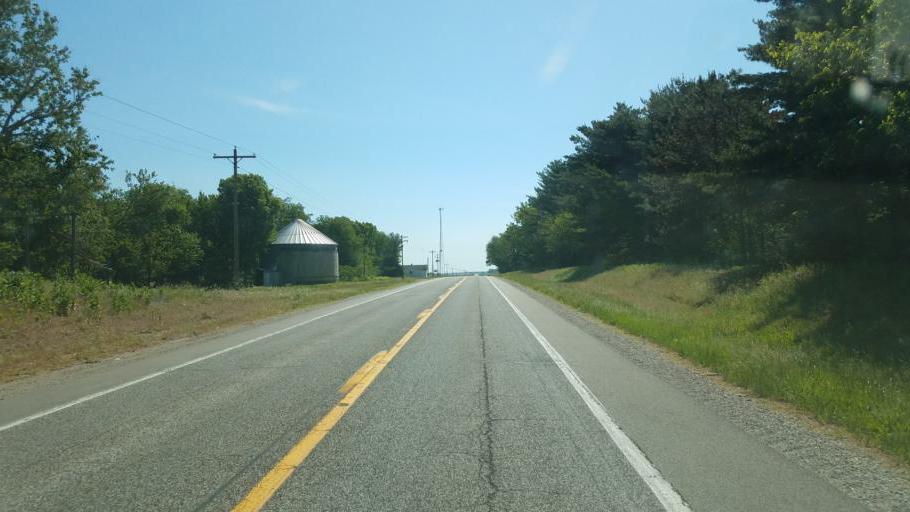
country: US
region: Illinois
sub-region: Mason County
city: Manito
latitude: 40.3035
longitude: -89.7810
